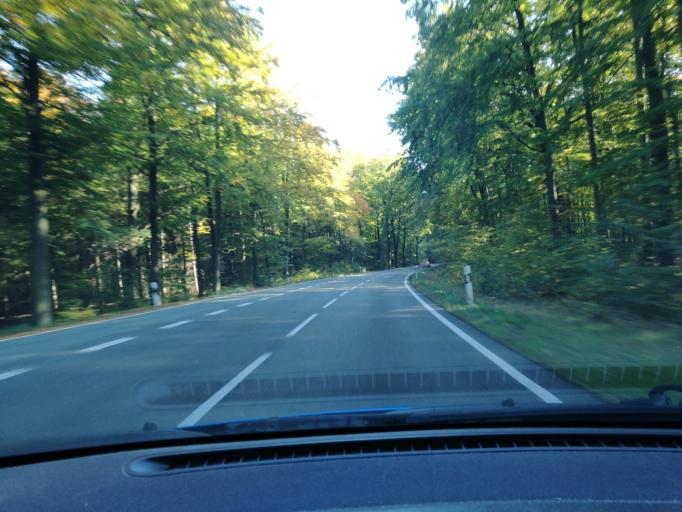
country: DE
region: Lower Saxony
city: Gohrde
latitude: 53.1457
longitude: 10.8697
